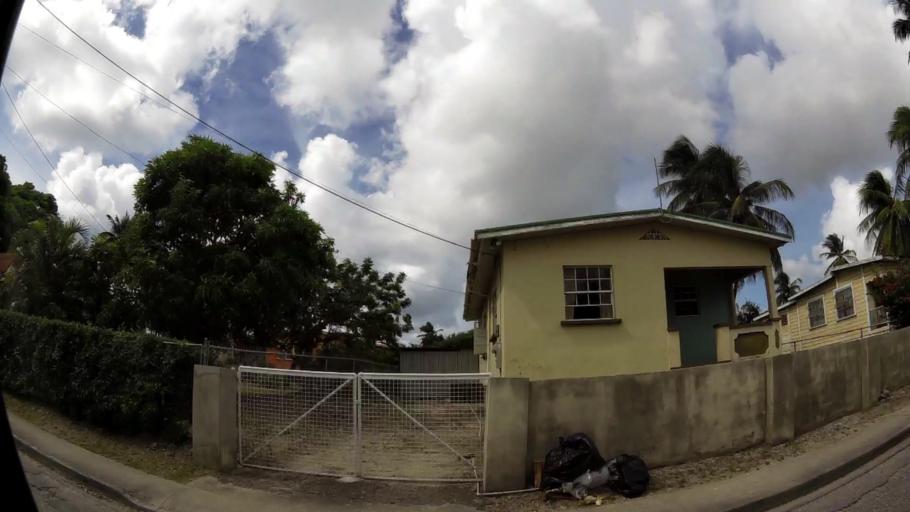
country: BB
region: Saint Michael
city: Bridgetown
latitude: 13.1206
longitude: -59.6177
